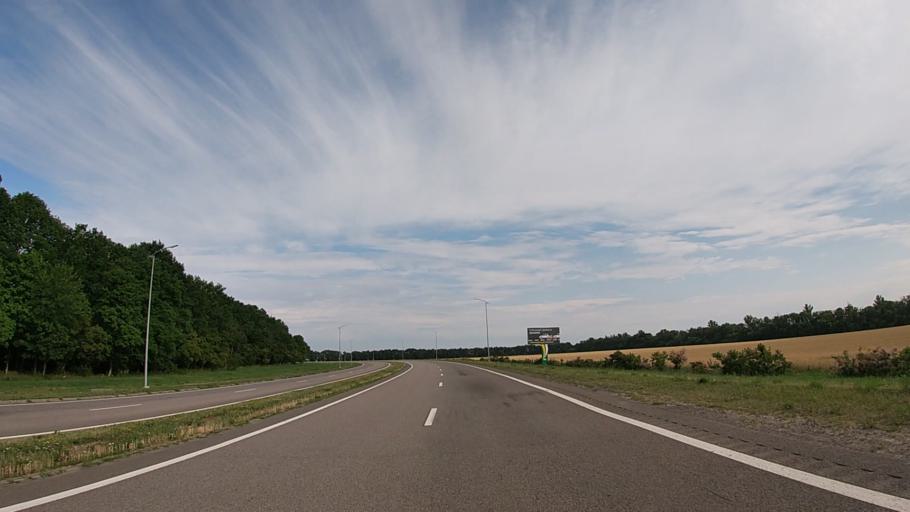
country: RU
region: Belgorod
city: Borisovka
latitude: 50.7591
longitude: 35.9642
